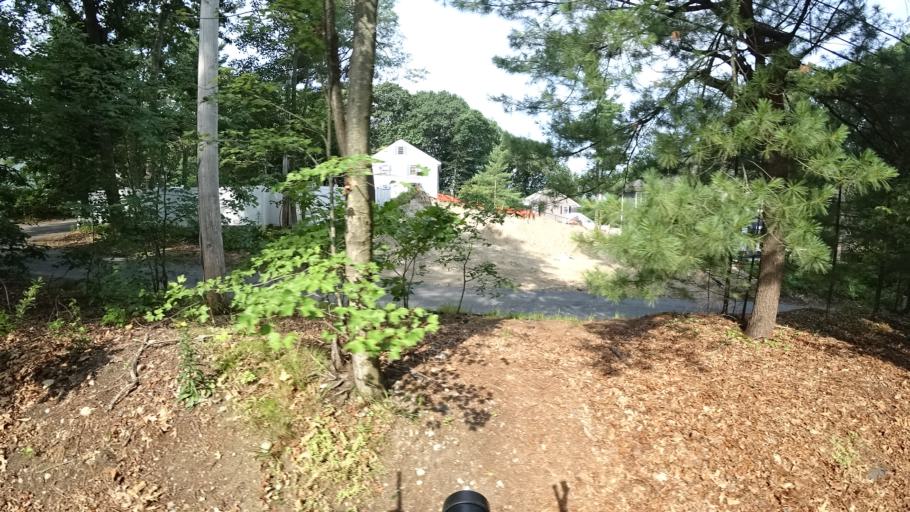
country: US
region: Massachusetts
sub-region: Norfolk County
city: Dedham
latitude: 42.2379
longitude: -71.1701
